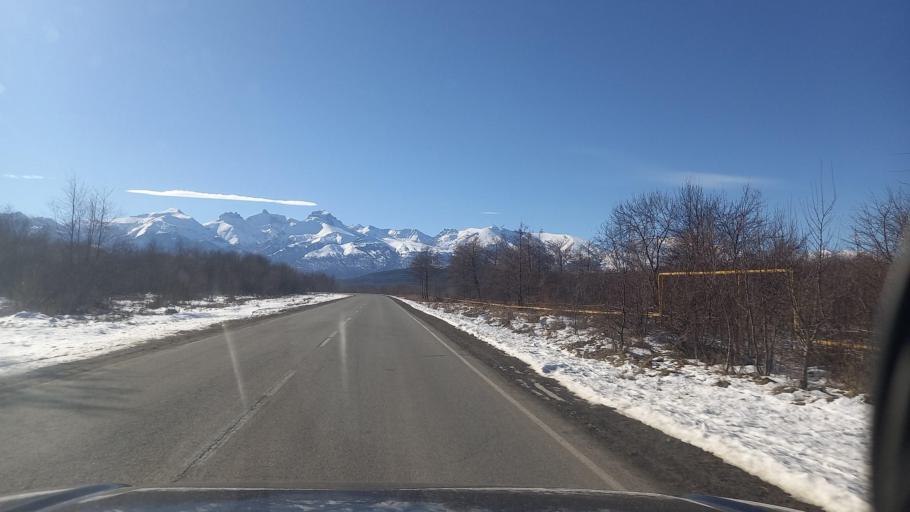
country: RU
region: North Ossetia
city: Chikola
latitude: 43.1537
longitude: 43.8413
